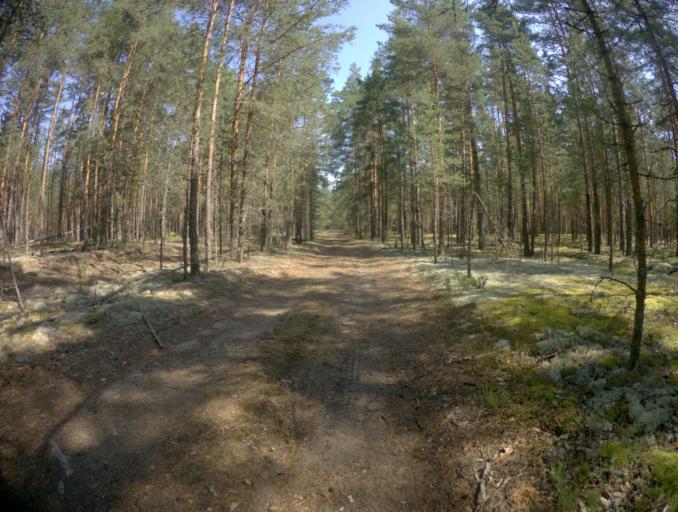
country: RU
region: Ivanovo
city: Talitsy
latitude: 56.3984
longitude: 42.2656
